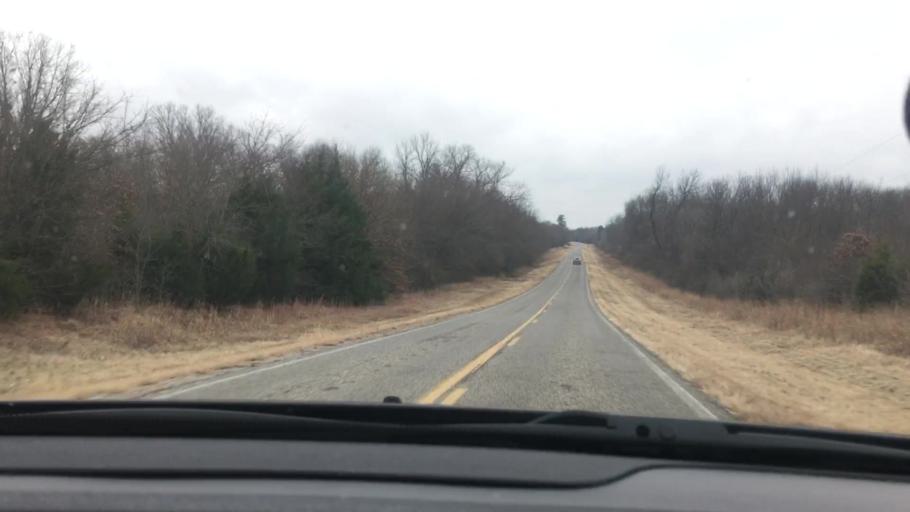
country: US
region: Oklahoma
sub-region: Johnston County
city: Tishomingo
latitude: 34.2181
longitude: -96.6361
